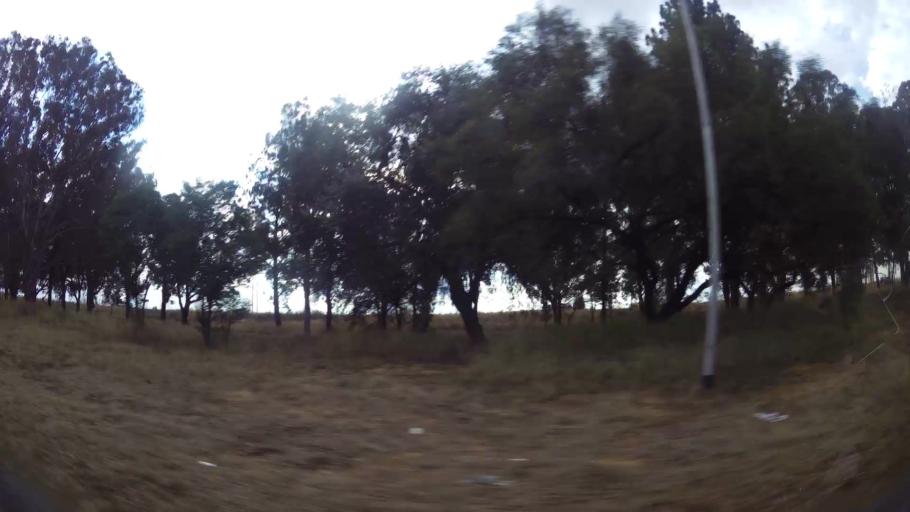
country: ZA
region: Orange Free State
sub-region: Fezile Dabi District Municipality
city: Sasolburg
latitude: -26.7899
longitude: 27.8186
